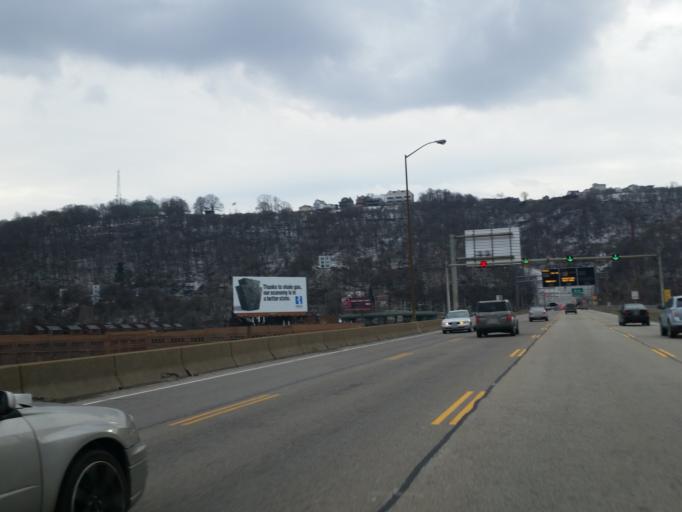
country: US
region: Pennsylvania
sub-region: Allegheny County
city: Pittsburgh
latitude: 40.4331
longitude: -79.9966
